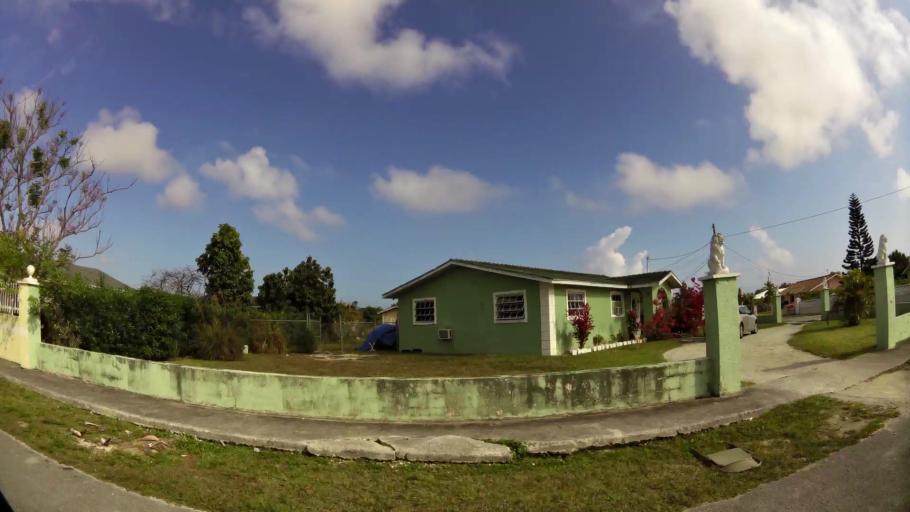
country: BS
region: Freeport
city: Lucaya
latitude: 26.5311
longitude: -78.6732
